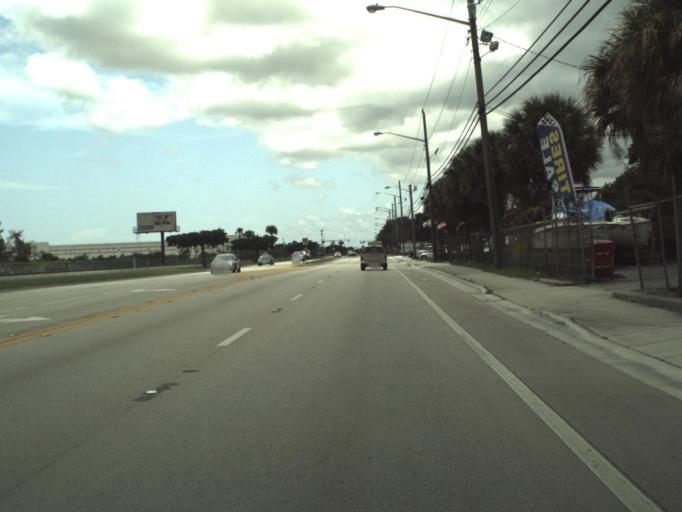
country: US
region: Florida
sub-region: Broward County
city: Pompano Beach Highlands
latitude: 26.2849
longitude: -80.1111
